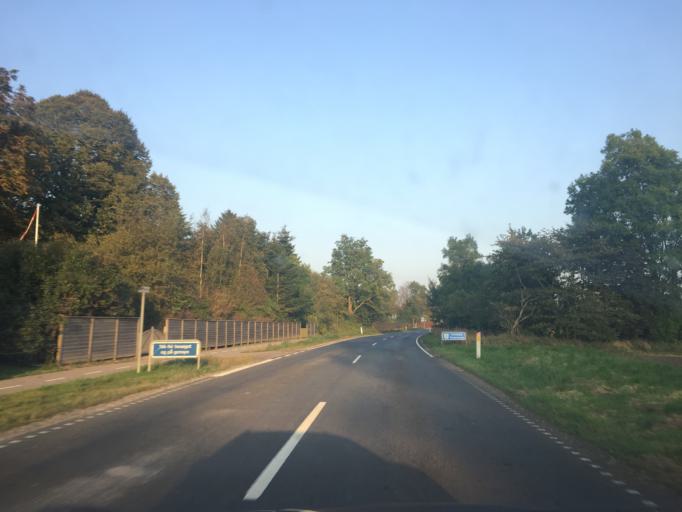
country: DK
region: Zealand
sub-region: Soro Kommune
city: Stenlille
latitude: 55.5435
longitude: 11.6814
